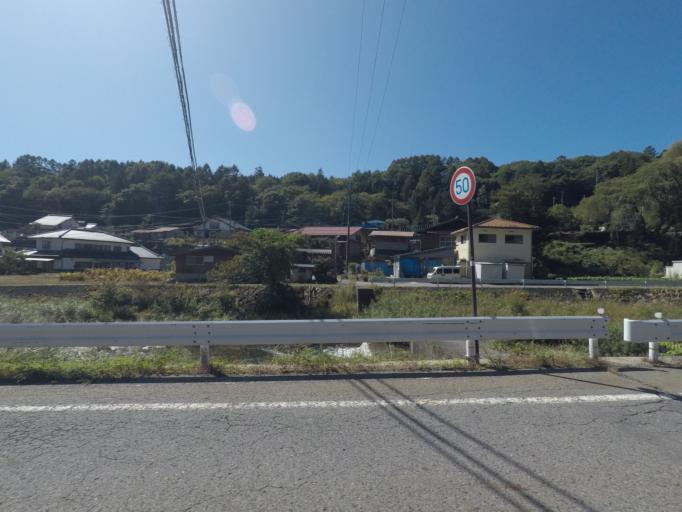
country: JP
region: Nagano
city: Tatsuno
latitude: 35.9791
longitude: 137.7471
